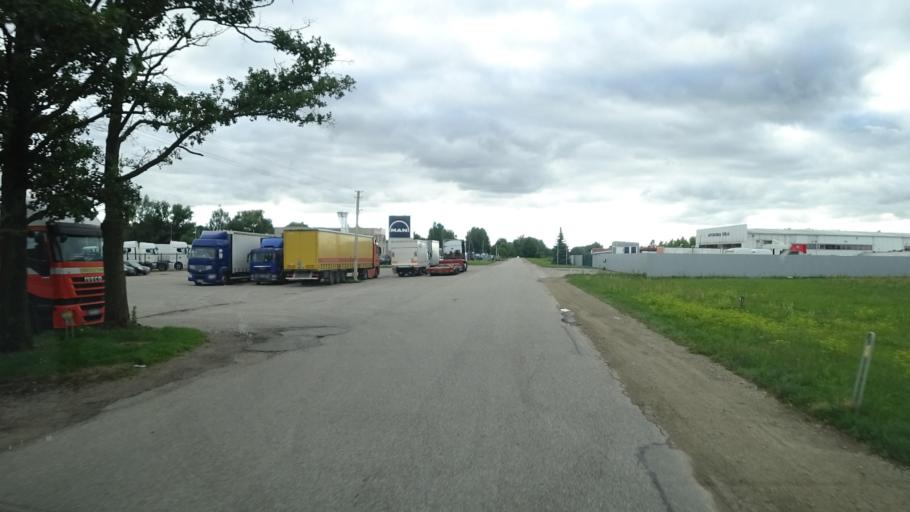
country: LT
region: Marijampoles apskritis
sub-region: Marijampole Municipality
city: Marijampole
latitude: 54.5813
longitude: 23.3743
